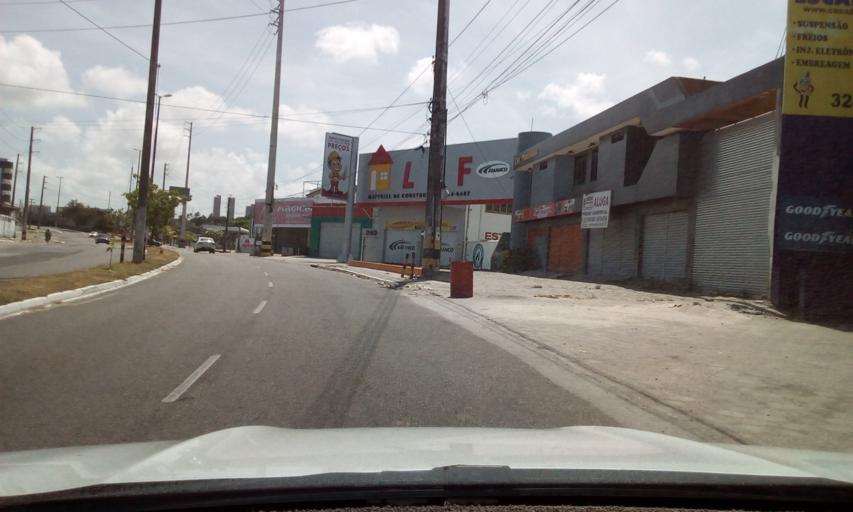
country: BR
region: Paraiba
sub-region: Joao Pessoa
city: Joao Pessoa
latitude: -7.0984
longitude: -34.8595
